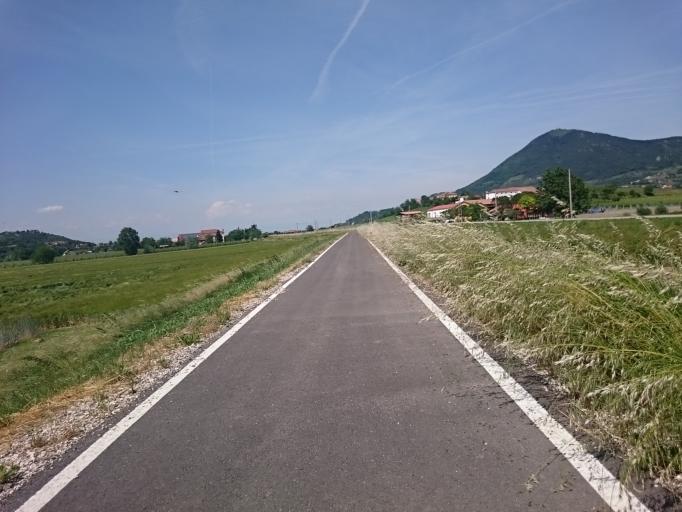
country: IT
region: Veneto
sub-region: Provincia di Padova
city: Vo
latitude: 45.3345
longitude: 11.6225
